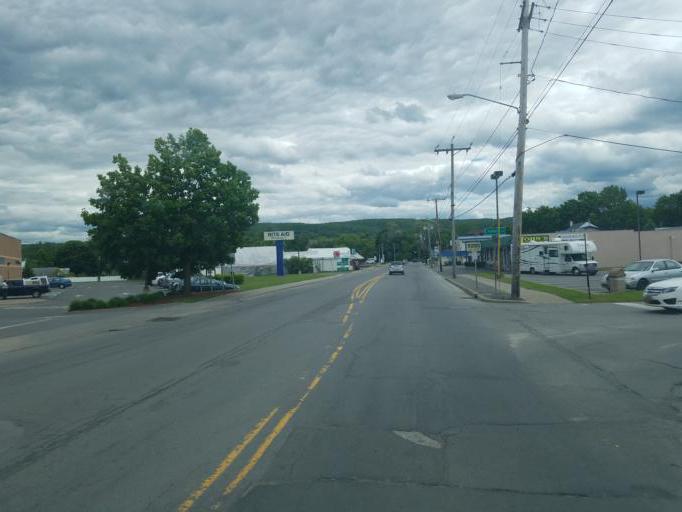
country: US
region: New York
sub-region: Herkimer County
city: Herkimer
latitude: 43.0222
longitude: -74.9927
